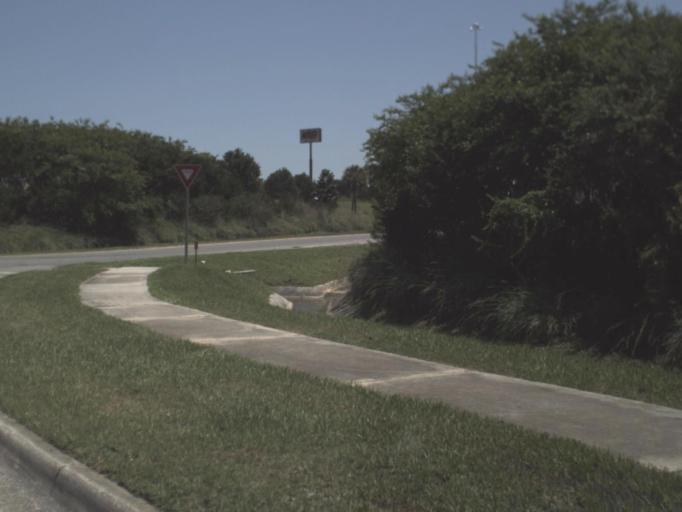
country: US
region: Florida
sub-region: Columbia County
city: Lake City
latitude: 30.1797
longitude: -82.6900
